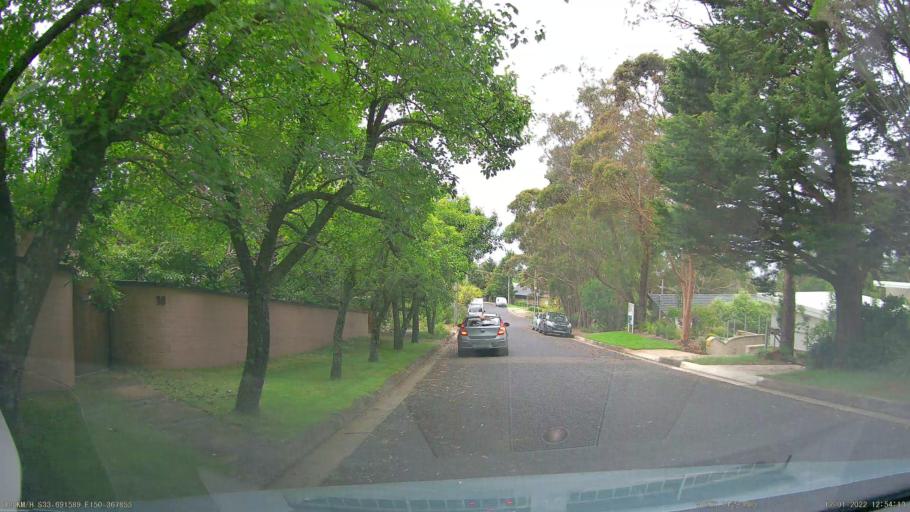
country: AU
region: New South Wales
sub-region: Blue Mountains Municipality
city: Leura
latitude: -33.6915
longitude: 150.3680
